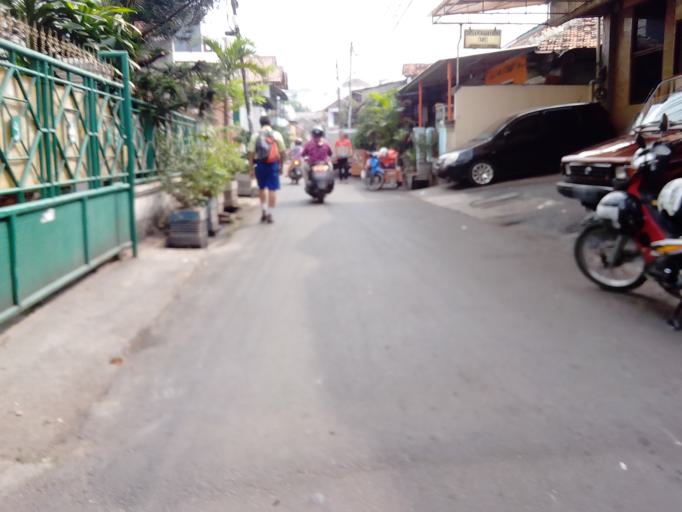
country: ID
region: Jakarta Raya
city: Jakarta
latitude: -6.1974
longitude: 106.8064
